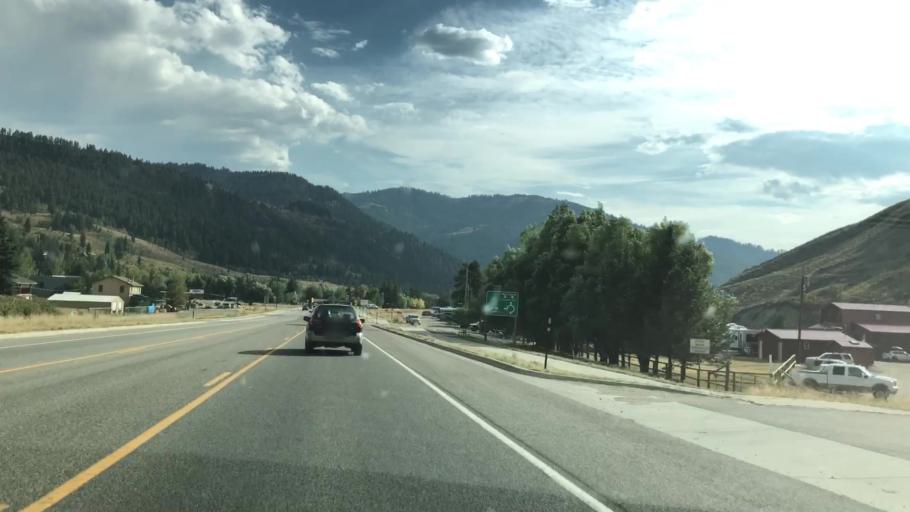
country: US
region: Wyoming
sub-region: Teton County
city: Hoback
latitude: 43.3257
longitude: -110.7296
